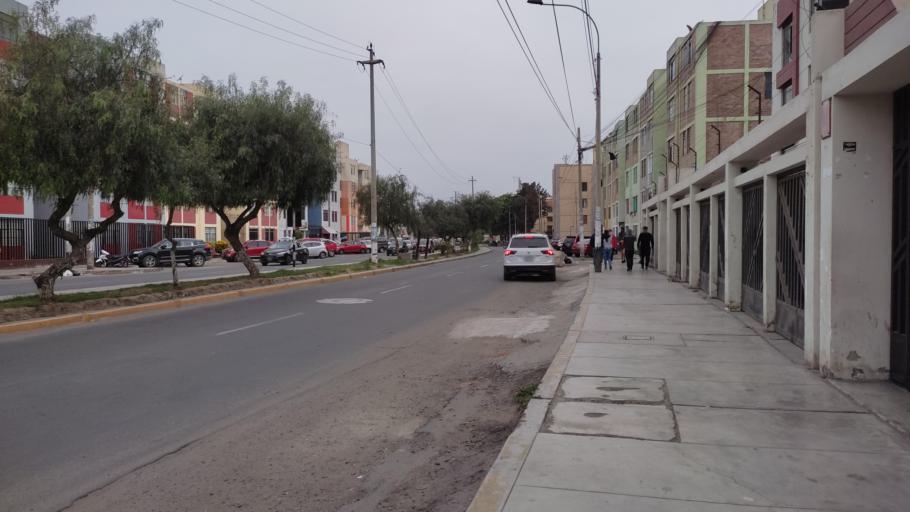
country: PE
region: La Libertad
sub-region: Provincia de Trujillo
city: Trujillo
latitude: -8.1243
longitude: -79.0298
